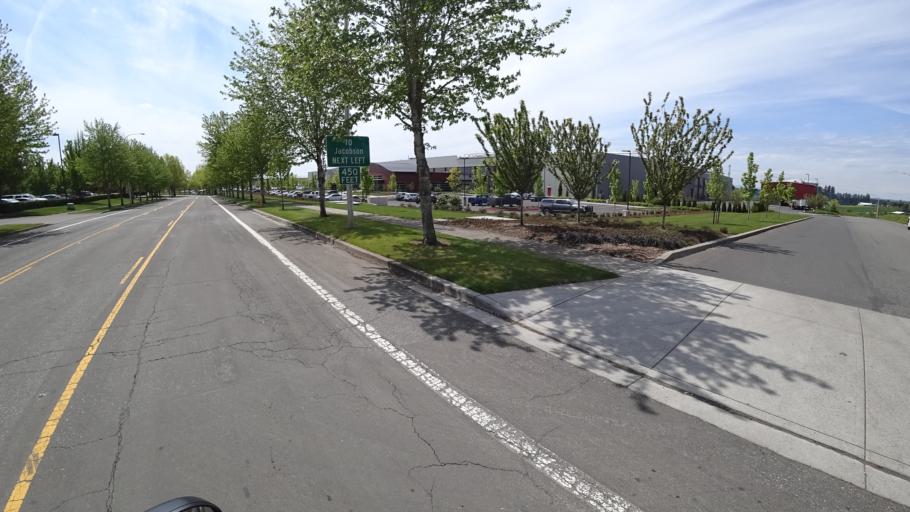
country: US
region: Oregon
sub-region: Washington County
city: Rockcreek
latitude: 45.5714
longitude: -122.9084
